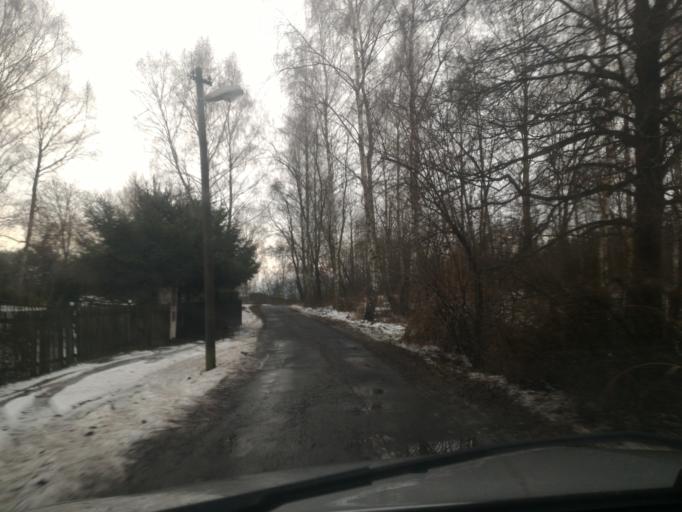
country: DE
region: Saxony
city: Leutersdorf
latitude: 50.9174
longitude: 14.6511
